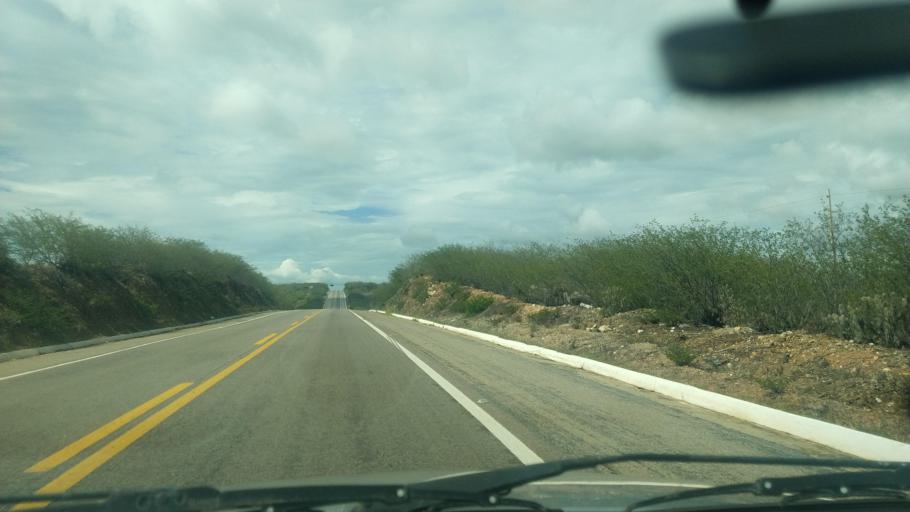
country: BR
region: Rio Grande do Norte
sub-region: Currais Novos
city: Currais Novos
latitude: -6.2202
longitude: -36.4272
